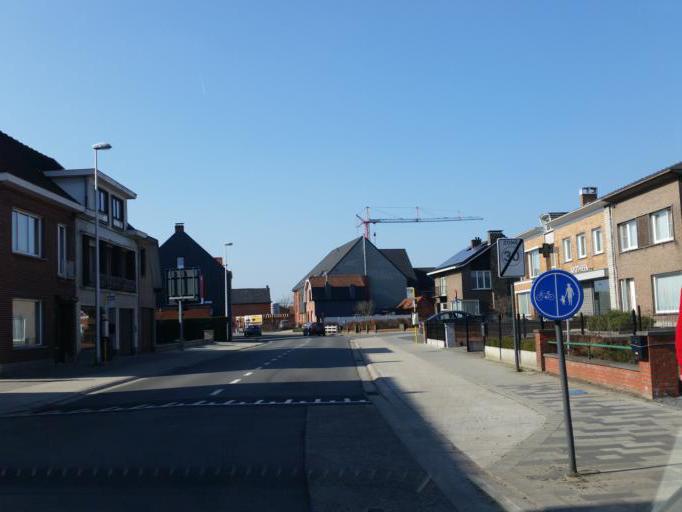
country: BE
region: Flanders
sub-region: Provincie Oost-Vlaanderen
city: Wachtebeke
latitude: 51.1713
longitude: 3.8579
